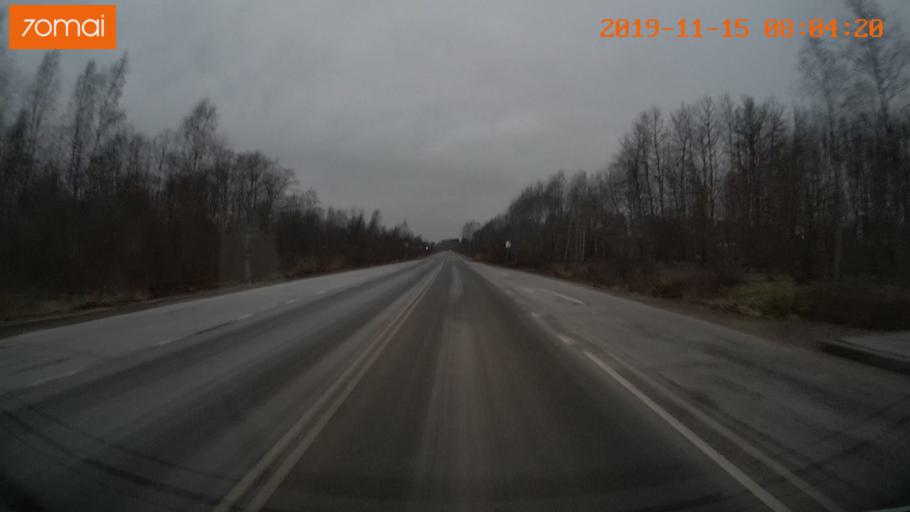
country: RU
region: Vologda
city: Cherepovets
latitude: 59.0072
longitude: 38.0779
